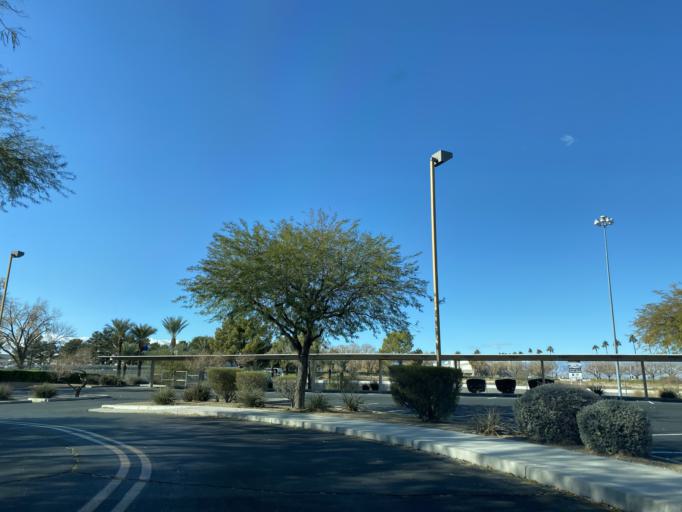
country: US
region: Nevada
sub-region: Clark County
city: Paradise
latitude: 36.0705
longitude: -115.1454
